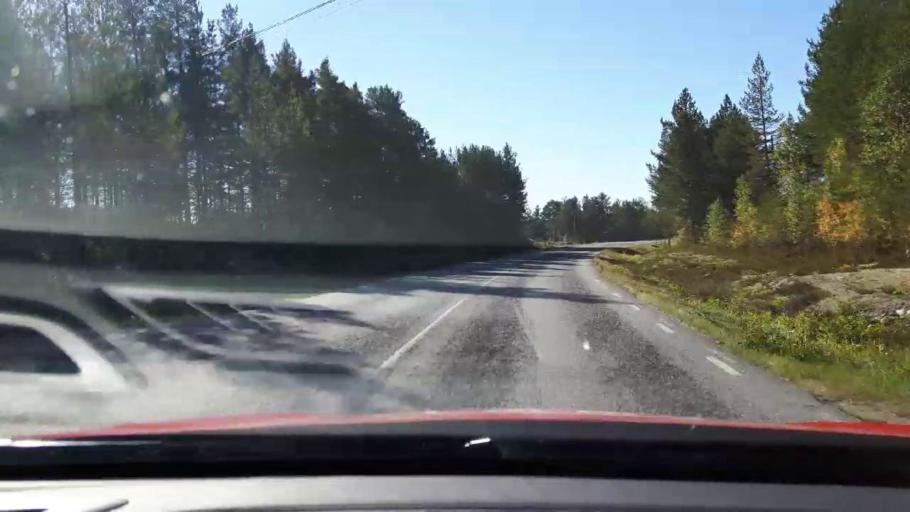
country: SE
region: Jaemtland
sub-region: Harjedalens Kommun
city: Sveg
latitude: 62.3222
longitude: 14.0615
